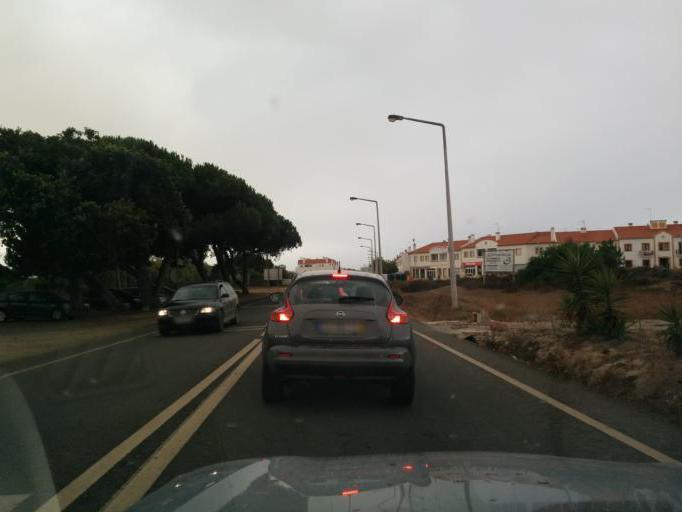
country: PT
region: Beja
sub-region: Odemira
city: Vila Nova de Milfontes
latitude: 37.7325
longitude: -8.7731
